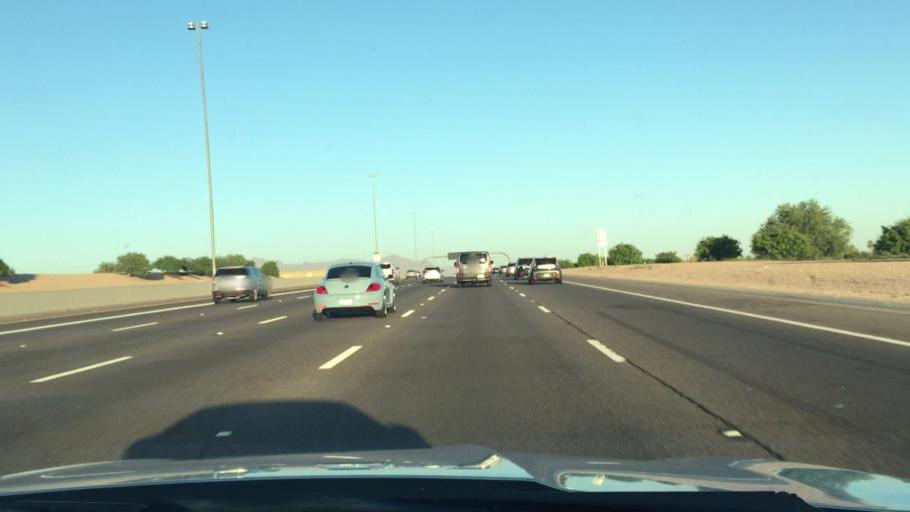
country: US
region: Arizona
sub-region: Maricopa County
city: Gilbert
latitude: 33.3864
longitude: -111.7058
